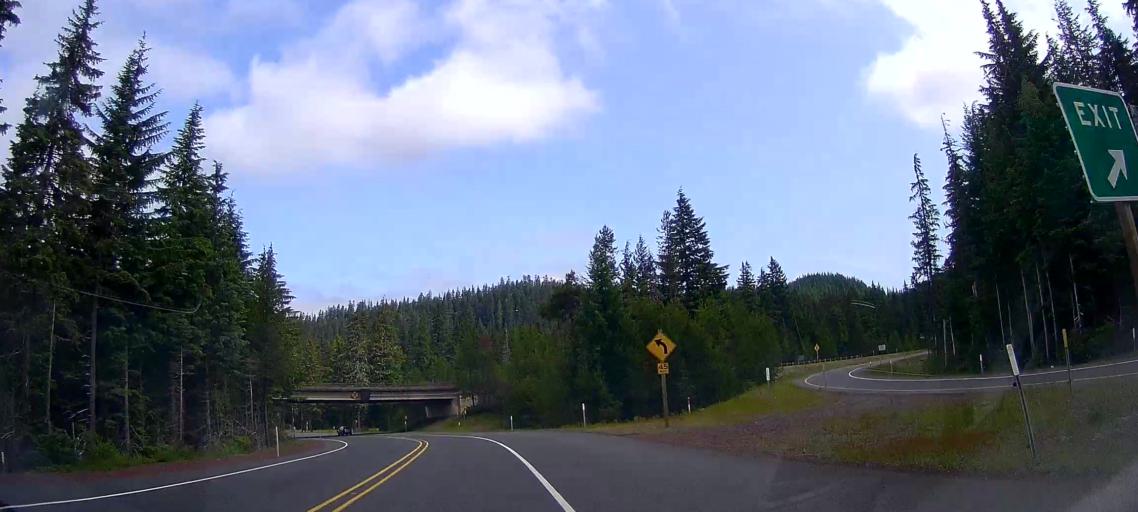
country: US
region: Oregon
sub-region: Clackamas County
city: Mount Hood Village
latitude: 45.2824
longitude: -121.7137
